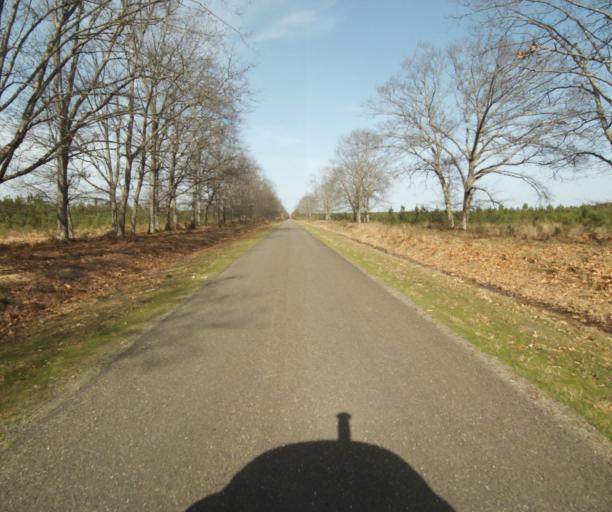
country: FR
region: Aquitaine
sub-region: Departement des Landes
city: Roquefort
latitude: 44.1624
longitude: -0.1664
